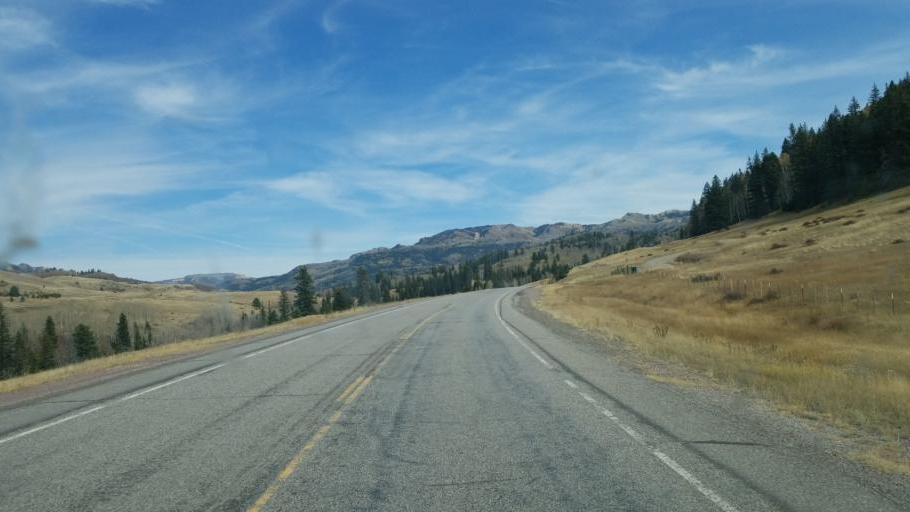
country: US
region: New Mexico
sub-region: Rio Arriba County
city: Chama
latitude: 36.9537
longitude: -106.5386
